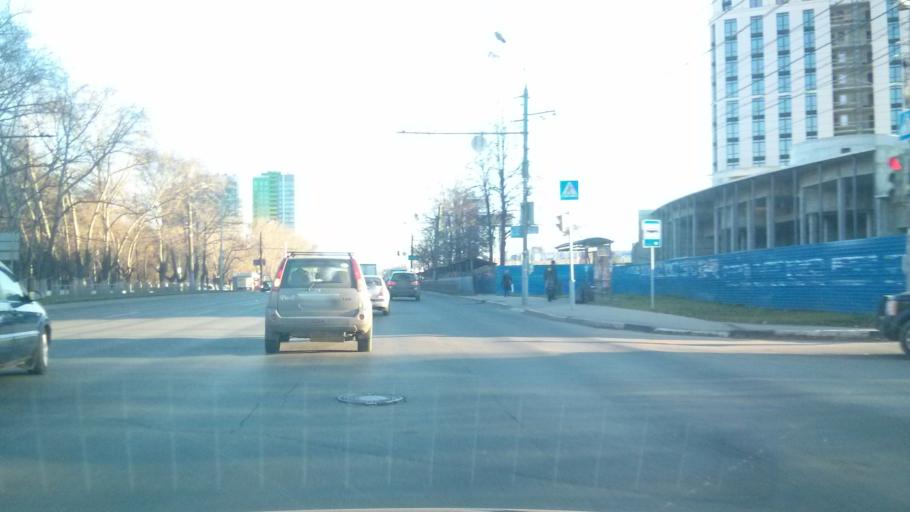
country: RU
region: Nizjnij Novgorod
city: Bor
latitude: 56.3111
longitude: 44.0743
